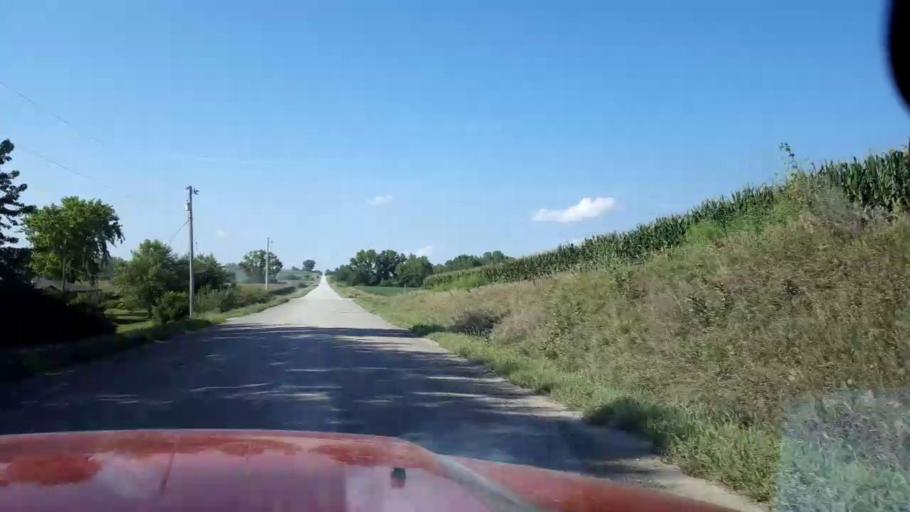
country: US
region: Iowa
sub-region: Pottawattamie County
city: Oakland
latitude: 41.2448
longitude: -95.5371
